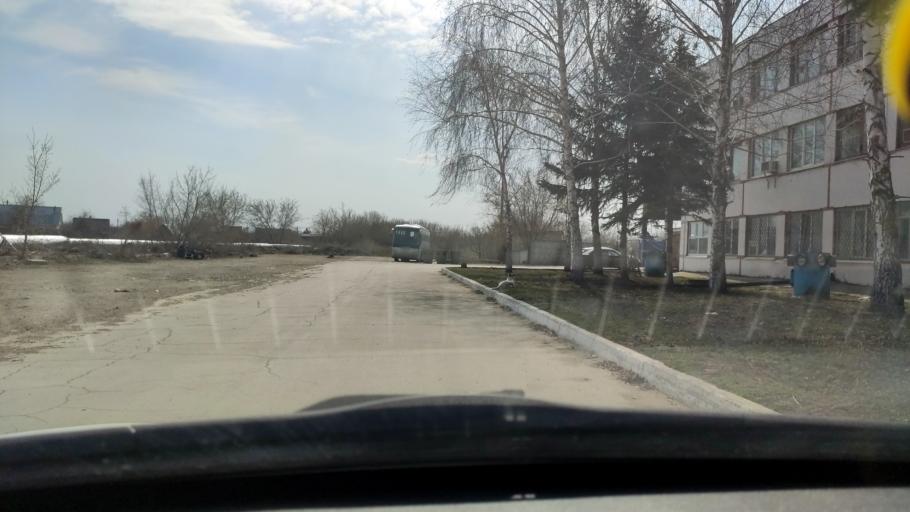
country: RU
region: Samara
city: Tol'yatti
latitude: 53.5451
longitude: 49.4324
